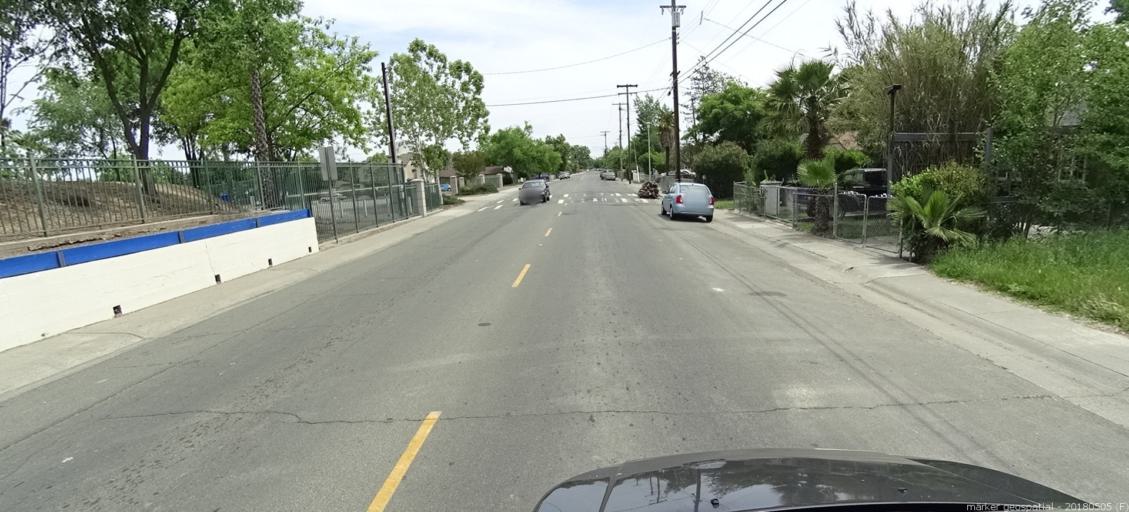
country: US
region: California
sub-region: Sacramento County
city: Rio Linda
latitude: 38.6329
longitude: -121.4328
